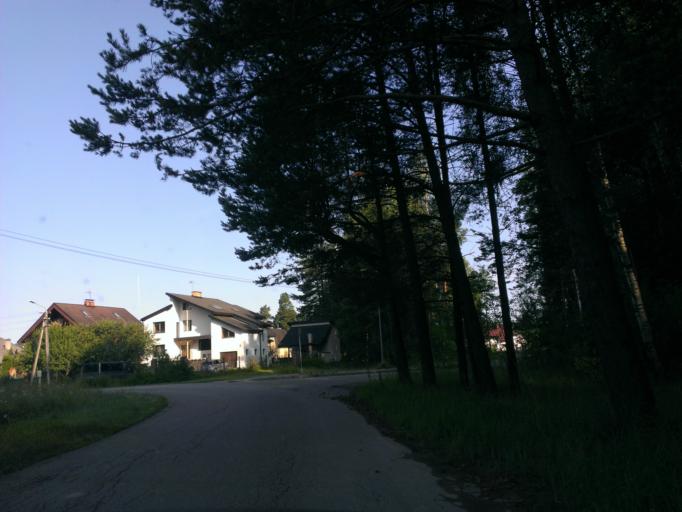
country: LV
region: Incukalns
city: Vangazi
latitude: 57.0934
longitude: 24.5607
